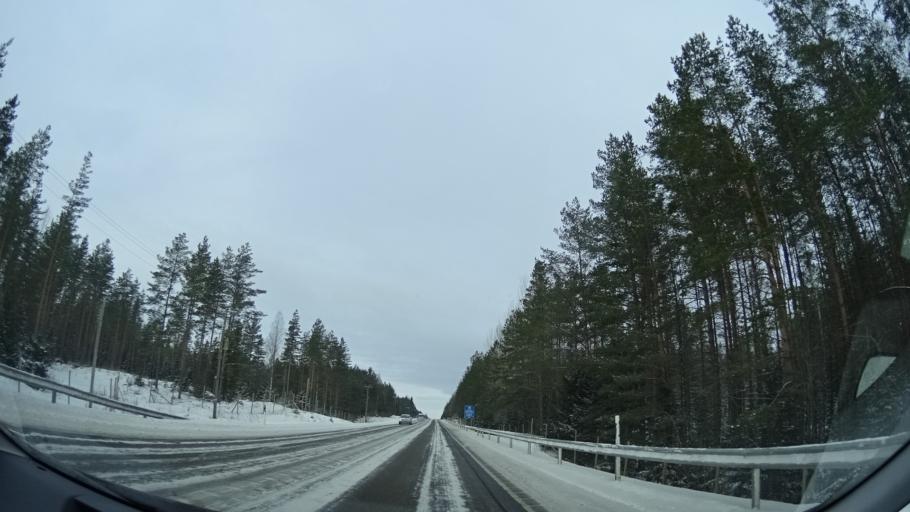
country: FI
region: Uusimaa
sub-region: Helsinki
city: Kaerkoelae
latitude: 60.6555
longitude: 23.8552
